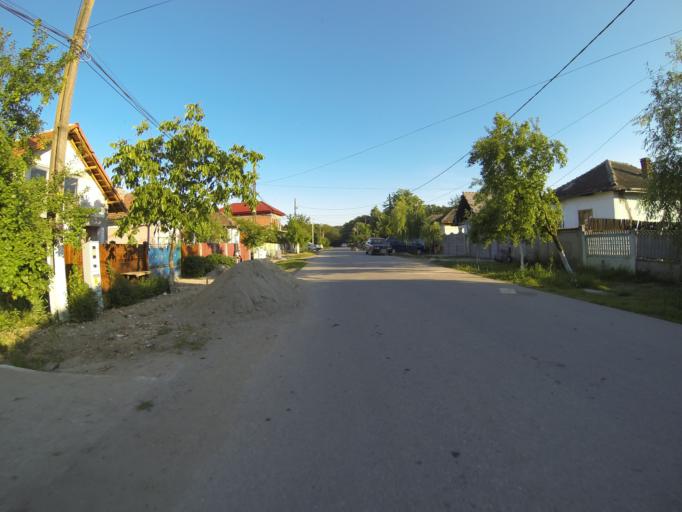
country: RO
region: Dolj
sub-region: Comuna Tuglui
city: Tuglui
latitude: 44.1782
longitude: 23.8157
